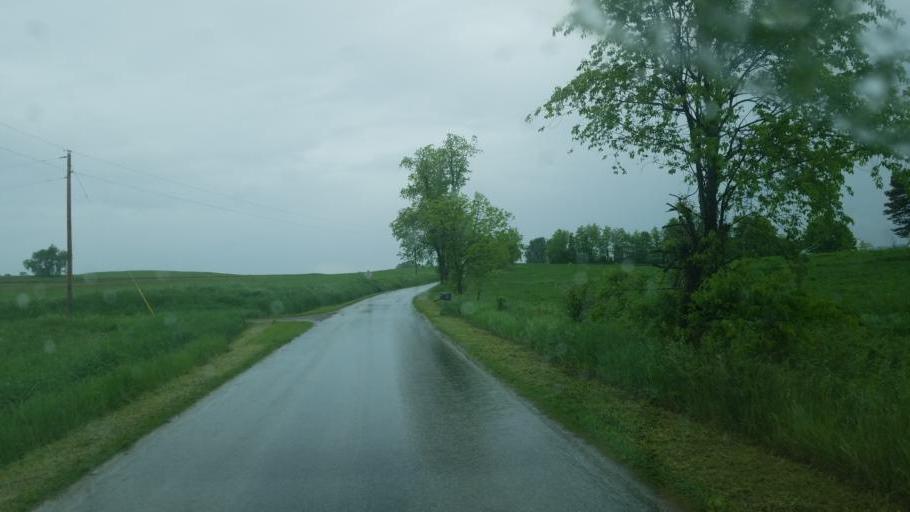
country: US
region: Ohio
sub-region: Wayne County
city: Apple Creek
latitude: 40.7276
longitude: -81.8631
